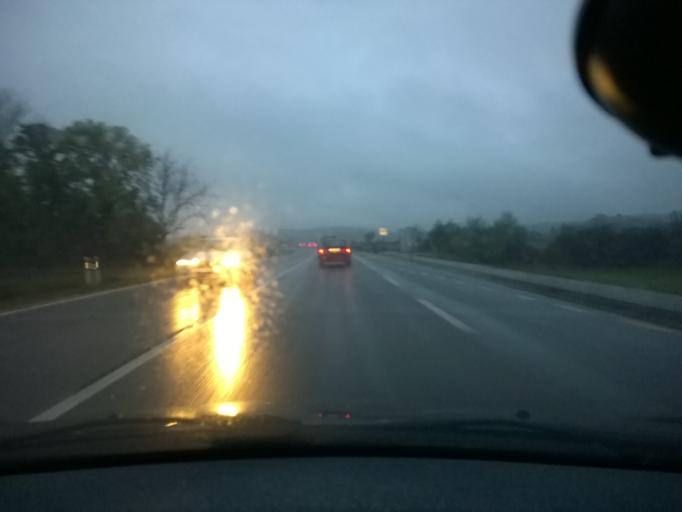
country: HR
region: Zagrebacka
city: Pojatno
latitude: 45.9089
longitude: 15.8144
